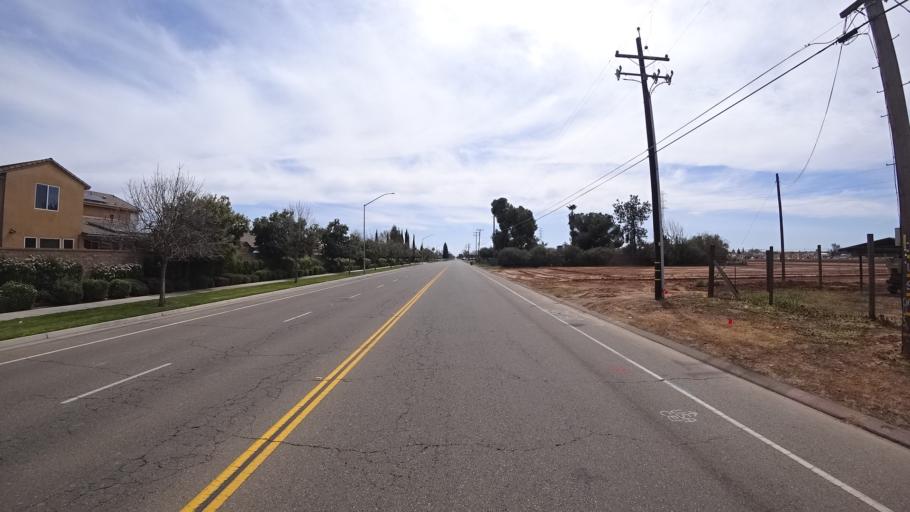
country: US
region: California
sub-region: Fresno County
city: West Park
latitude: 36.7973
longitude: -119.8984
